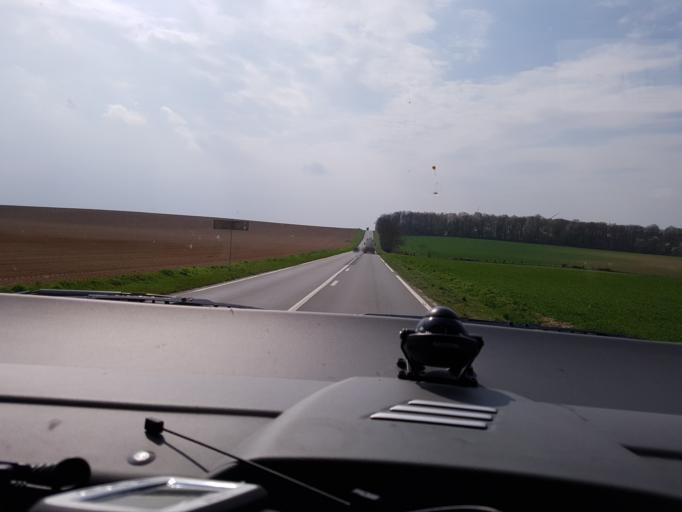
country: FR
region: Picardie
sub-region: Departement de l'Aisne
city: Crouy
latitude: 49.4433
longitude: 3.3579
